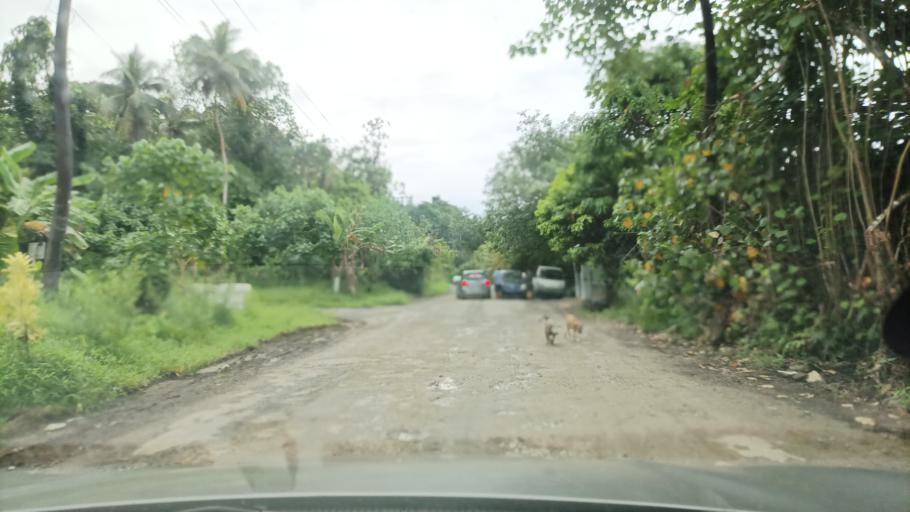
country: FM
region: Pohnpei
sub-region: Kolonia Municipality
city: Kolonia
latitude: 6.9308
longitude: 158.2781
